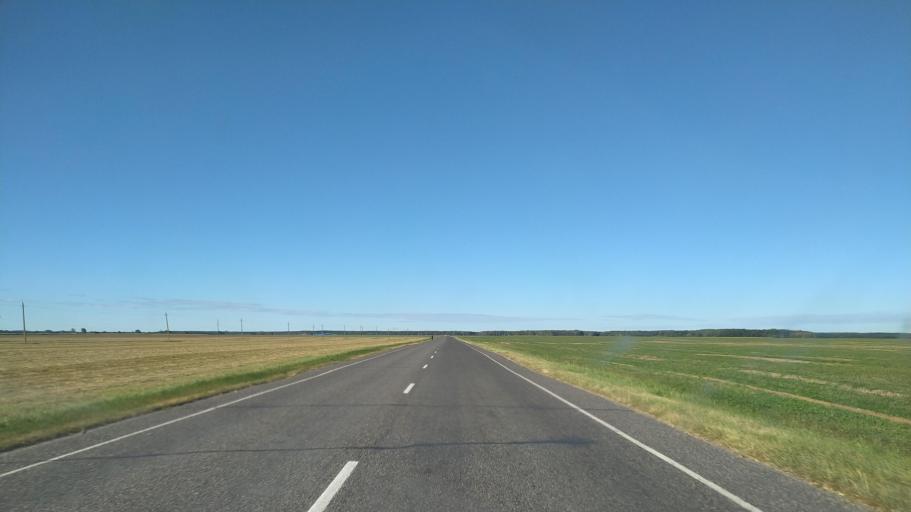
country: BY
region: Brest
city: Byaroza
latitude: 52.5153
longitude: 24.9106
